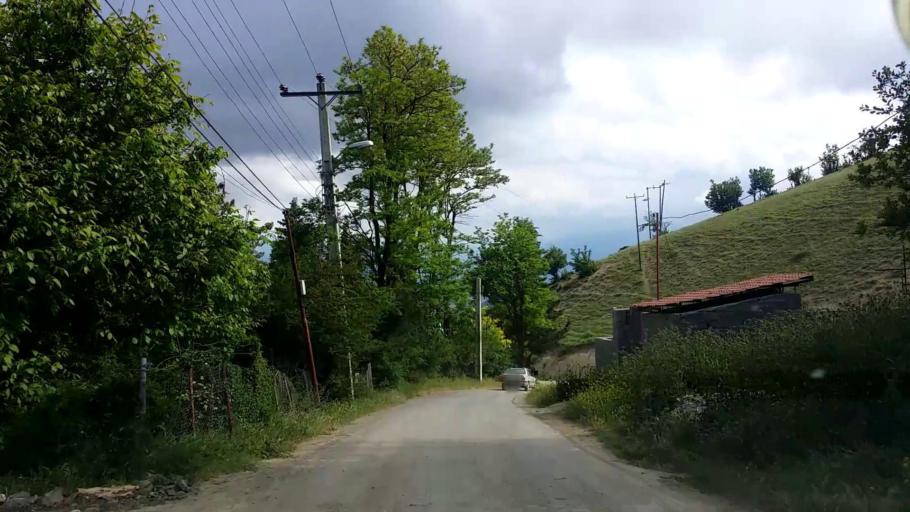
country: IR
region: Mazandaran
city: Chalus
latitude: 36.5556
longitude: 51.2893
